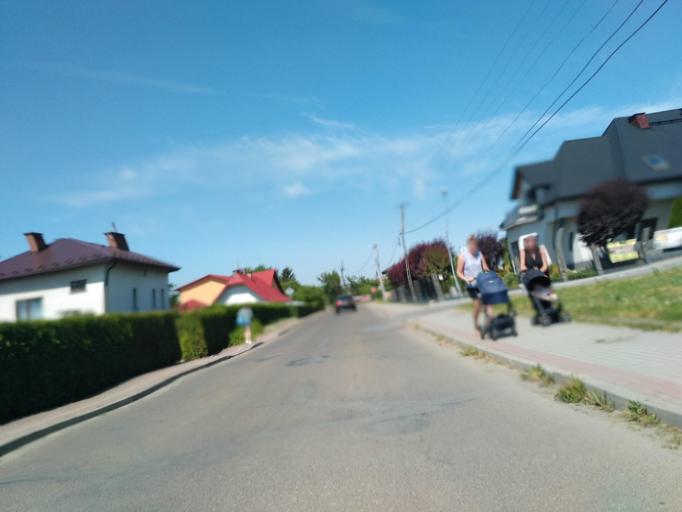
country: PL
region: Subcarpathian Voivodeship
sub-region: Powiat krosnienski
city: Korczyna
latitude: 49.7135
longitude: 21.7964
